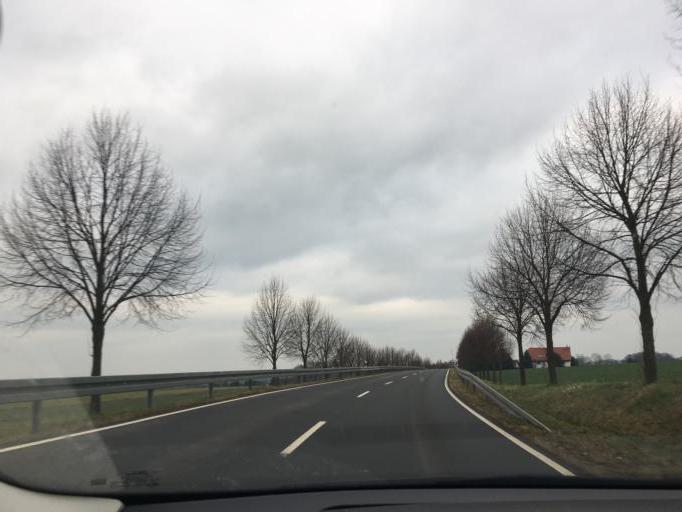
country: DE
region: Saxony
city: Hohenstein-Ernstthal
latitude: 50.8267
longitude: 12.7033
